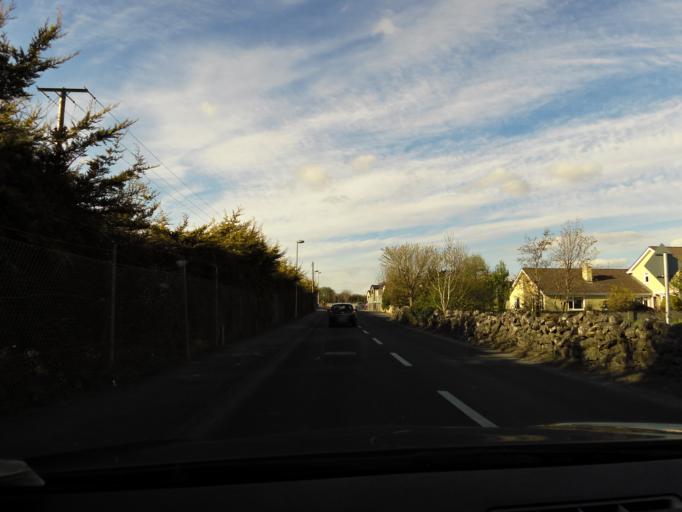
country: IE
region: Connaught
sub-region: County Galway
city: Athenry
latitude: 53.2946
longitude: -8.7431
